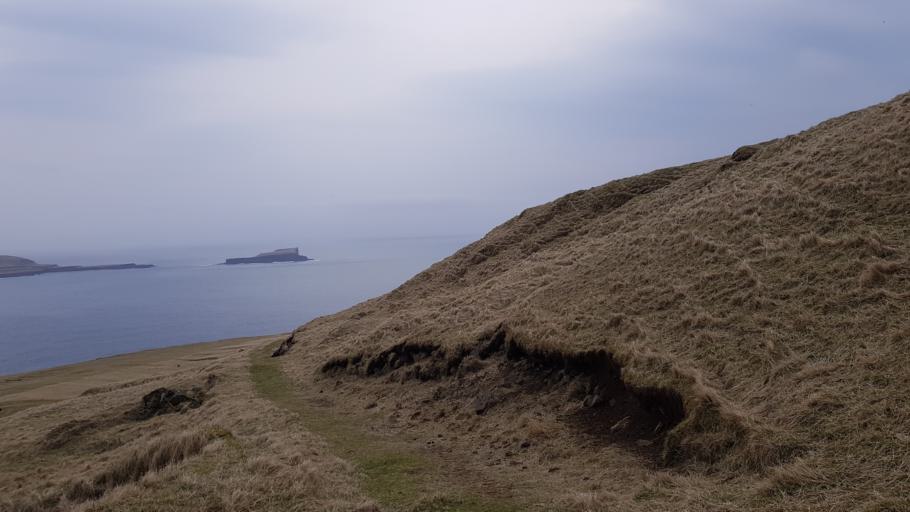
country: FO
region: Vagar
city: Sorvagur
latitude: 62.1119
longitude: -7.4420
